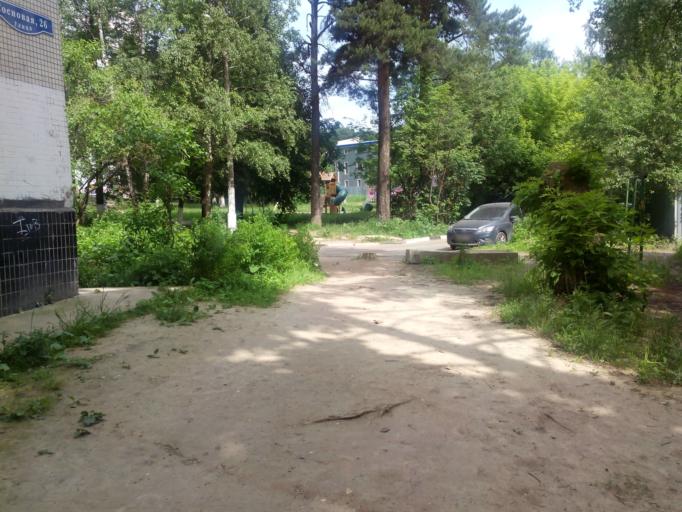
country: RU
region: Moskovskaya
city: Odintsovo
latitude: 55.6652
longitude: 37.2948
